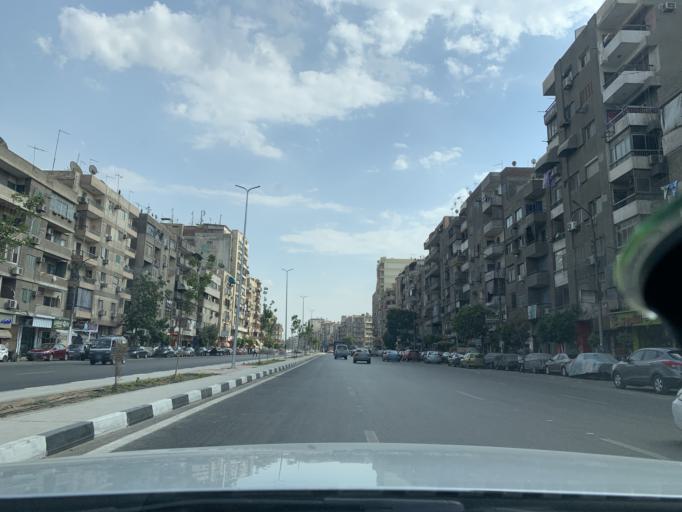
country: EG
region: Muhafazat al Qalyubiyah
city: Al Khankah
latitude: 30.1082
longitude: 31.3446
